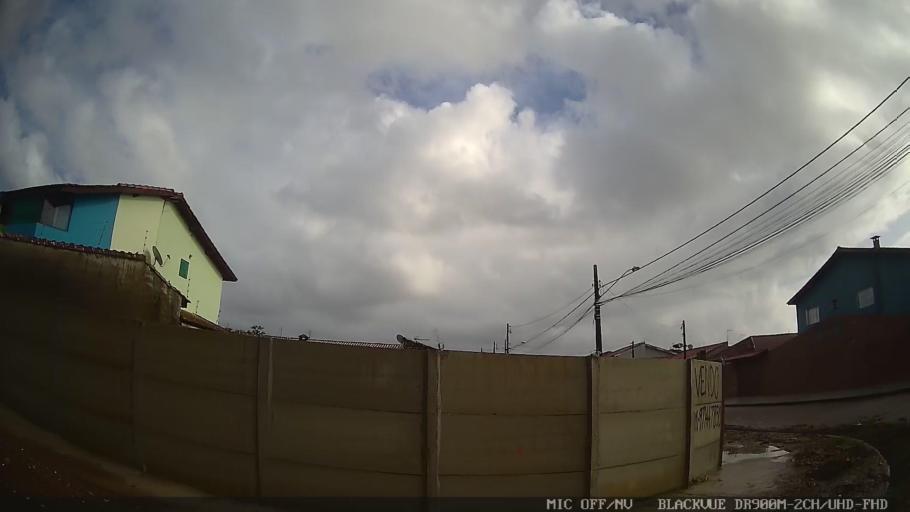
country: BR
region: Sao Paulo
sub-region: Itanhaem
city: Itanhaem
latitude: -24.1973
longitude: -46.8243
